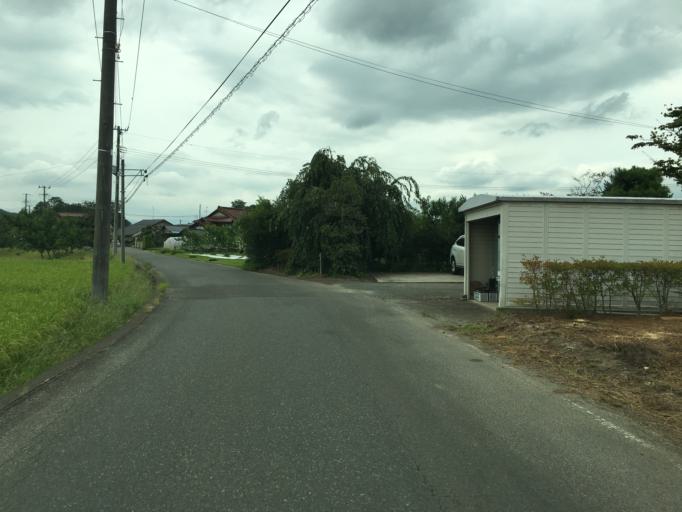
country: JP
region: Fukushima
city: Hobaramachi
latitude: 37.8175
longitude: 140.5426
